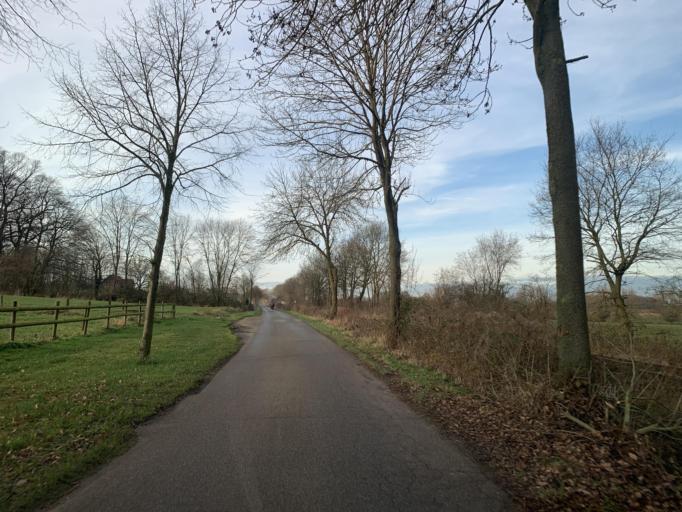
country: DE
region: North Rhine-Westphalia
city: Ludinghausen
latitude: 51.7897
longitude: 7.3885
